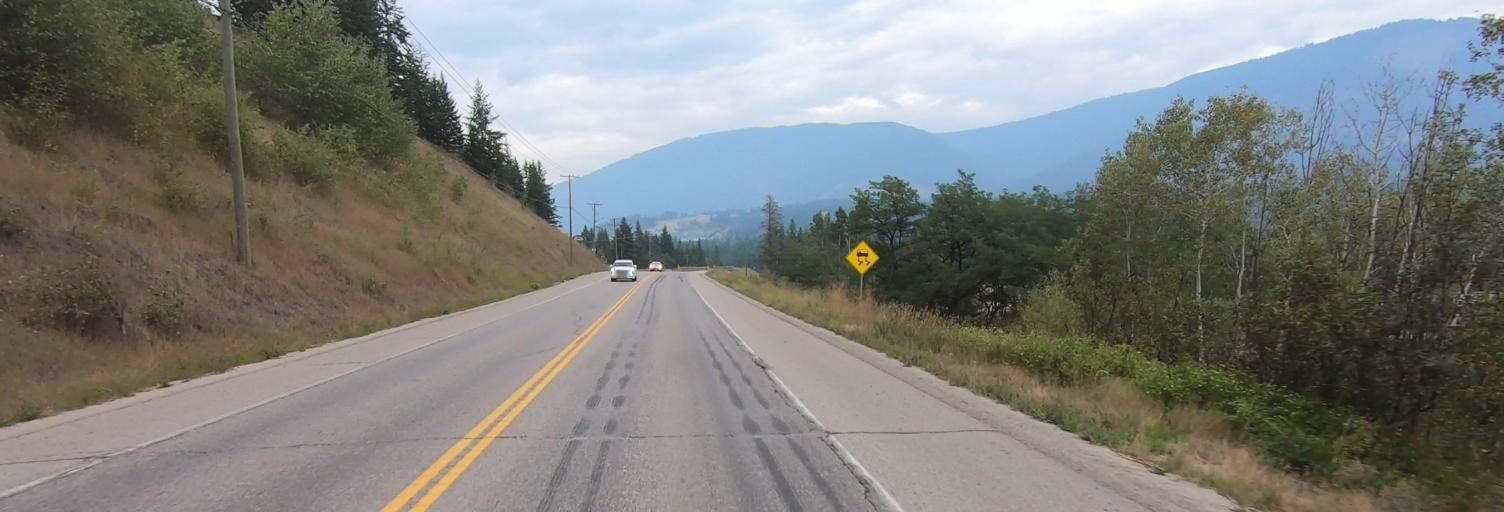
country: CA
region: British Columbia
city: Salmon Arm
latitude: 50.7832
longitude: -119.3358
